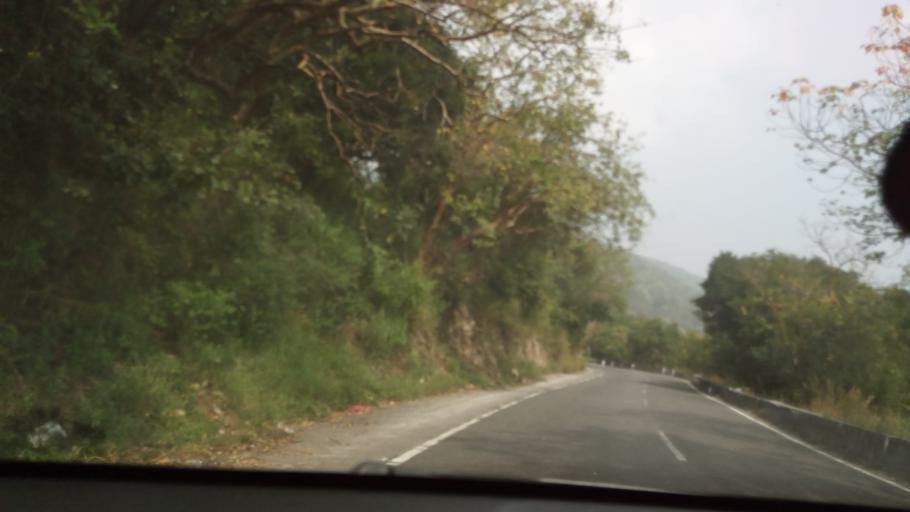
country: IN
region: Tamil Nadu
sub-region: Erode
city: Sathyamangalam
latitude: 11.5936
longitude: 77.1271
